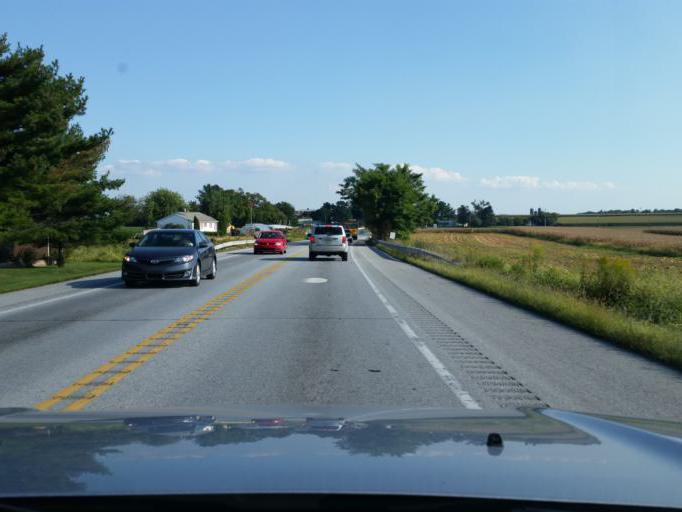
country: US
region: Pennsylvania
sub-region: Chester County
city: Atglen
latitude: 39.9322
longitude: -75.9523
